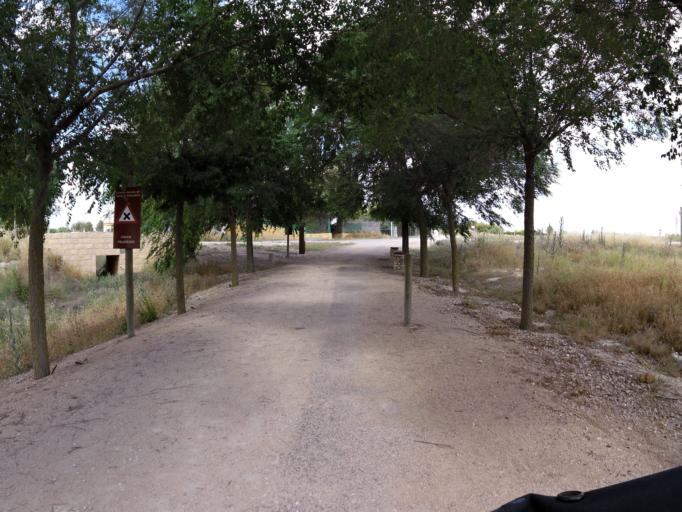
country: ES
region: Castille-La Mancha
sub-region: Provincia de Albacete
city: Albacete
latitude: 38.9618
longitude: -1.9600
